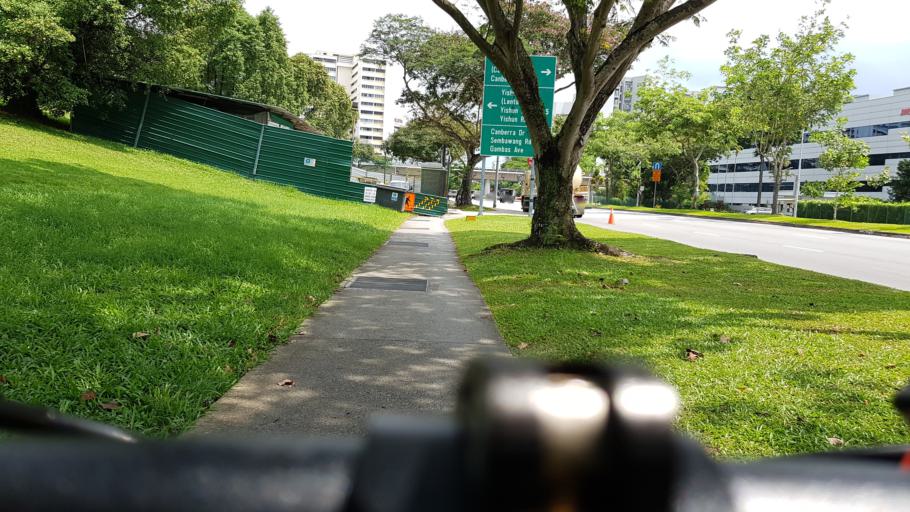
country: MY
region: Johor
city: Kampung Pasir Gudang Baru
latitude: 1.4388
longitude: 103.8347
